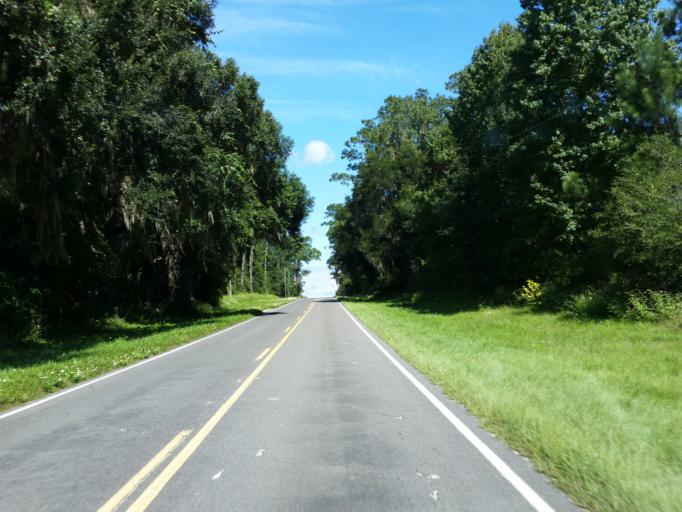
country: US
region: Florida
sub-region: Alachua County
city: Gainesville
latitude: 29.5852
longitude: -82.2395
